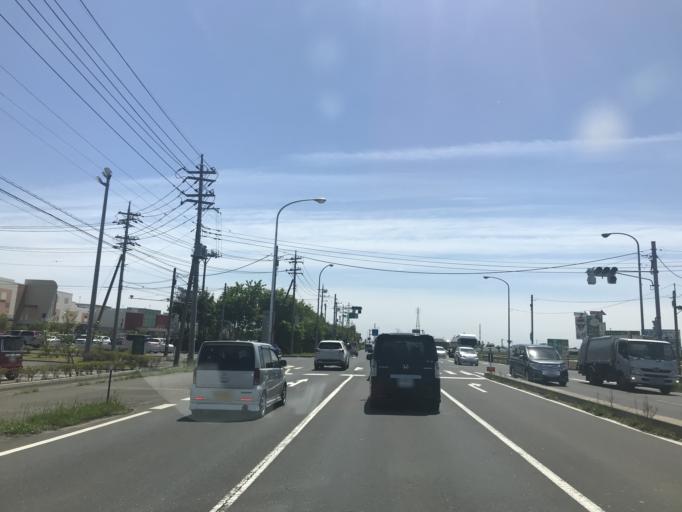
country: JP
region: Ibaraki
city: Ishige
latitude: 36.1931
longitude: 139.9873
